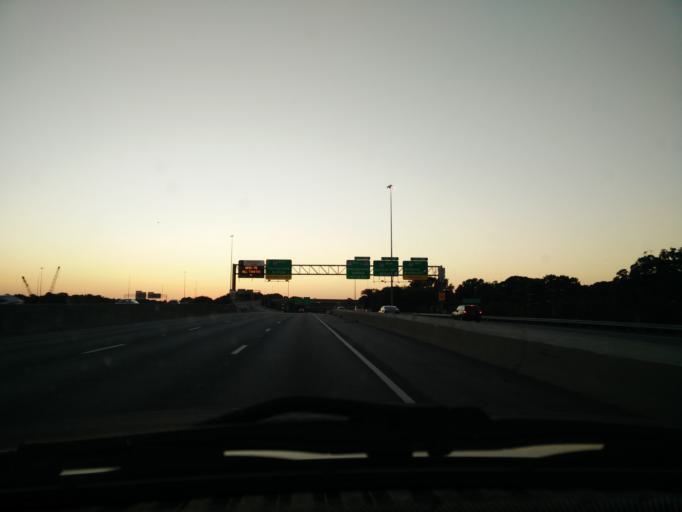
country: US
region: Virginia
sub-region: City of Chesapeake
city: Chesapeake
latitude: 36.8460
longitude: -76.1891
